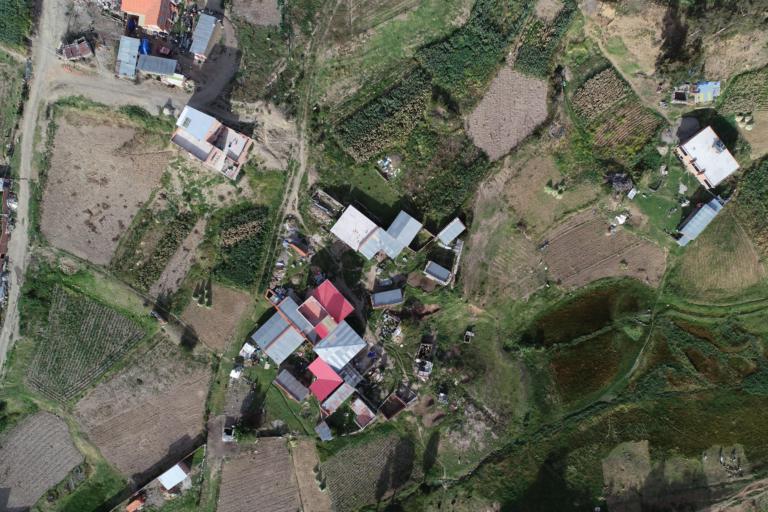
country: BO
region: La Paz
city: La Paz
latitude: -16.5461
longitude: -68.0014
